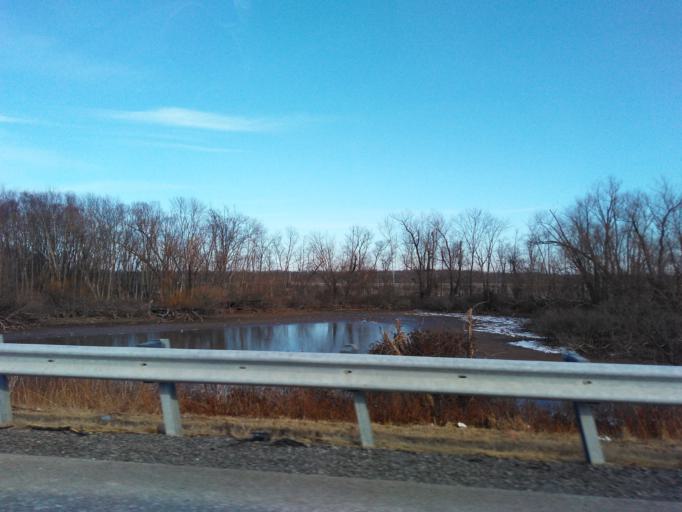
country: US
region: Illinois
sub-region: Jefferson County
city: Ina
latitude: 38.1058
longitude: -88.9116
